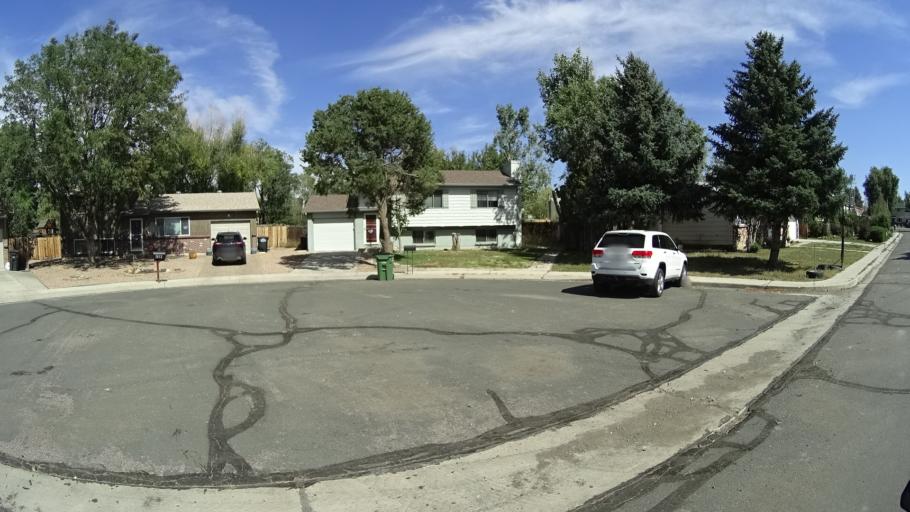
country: US
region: Colorado
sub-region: El Paso County
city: Cimarron Hills
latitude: 38.8993
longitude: -104.7551
